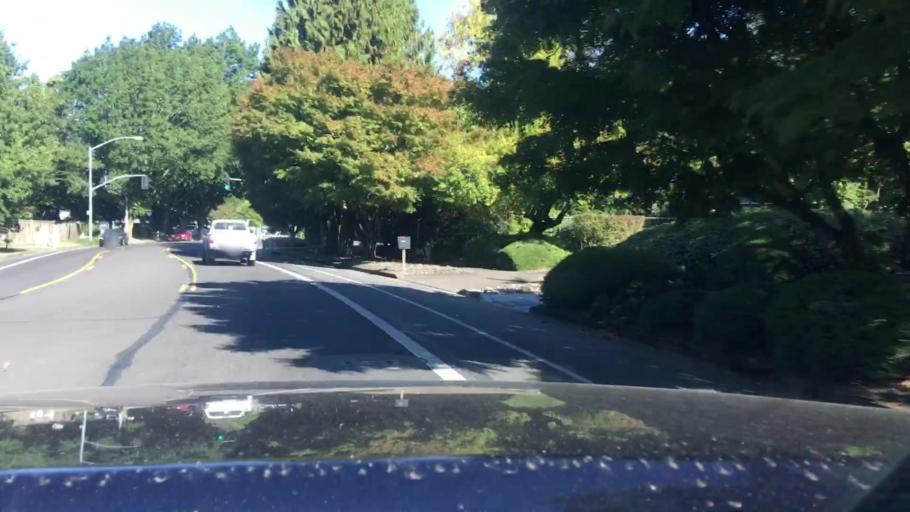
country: US
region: Oregon
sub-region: Lane County
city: Eugene
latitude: 44.0693
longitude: -123.0650
